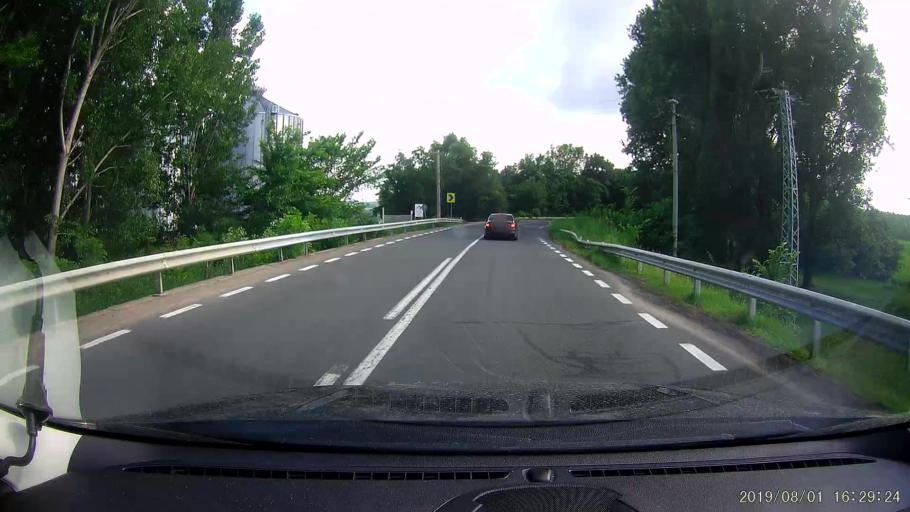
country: BG
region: Silistra
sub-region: Obshtina Silistra
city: Silistra
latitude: 44.1415
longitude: 27.2900
